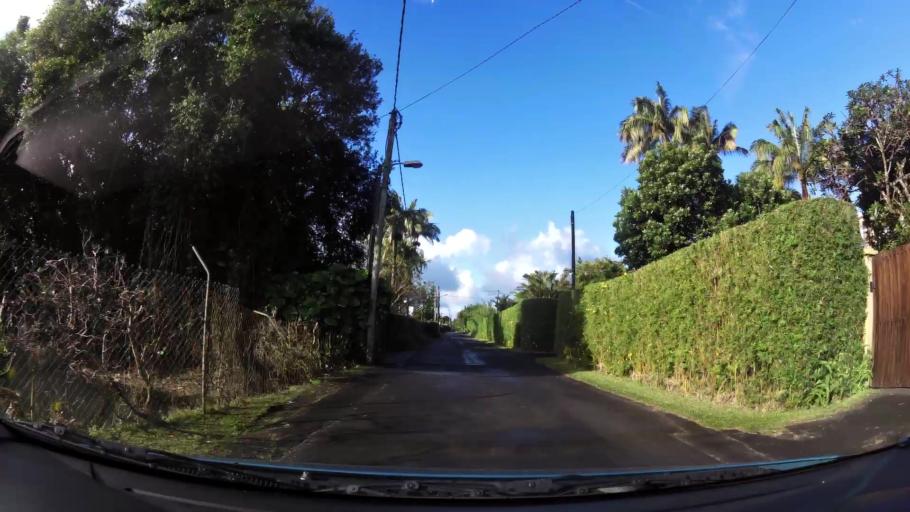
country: MU
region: Plaines Wilhems
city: Curepipe
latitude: -20.3175
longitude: 57.5047
